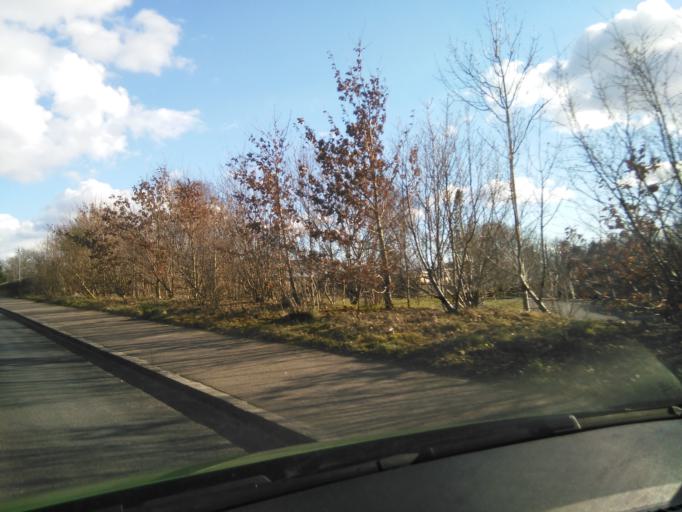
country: DK
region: Central Jutland
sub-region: Silkeborg Kommune
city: Silkeborg
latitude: 56.1842
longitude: 9.5154
